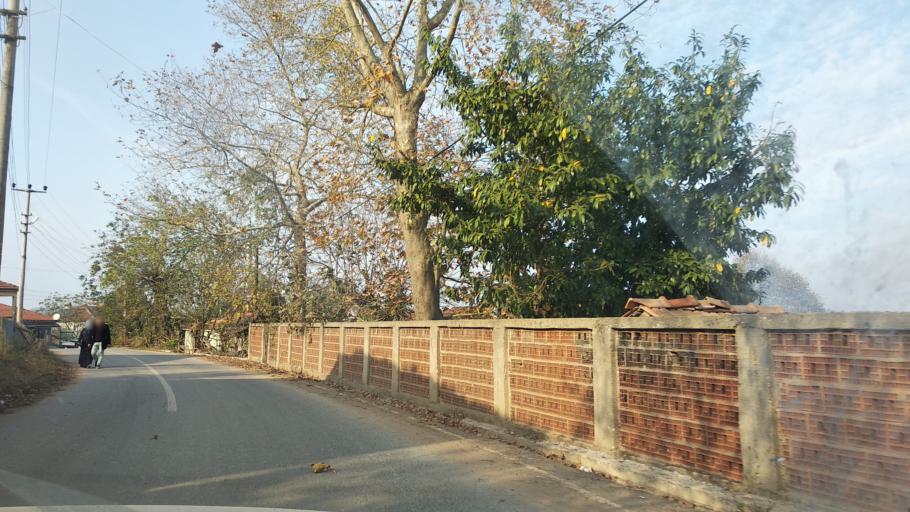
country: TR
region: Sakarya
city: Karasu
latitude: 41.0824
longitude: 30.6080
